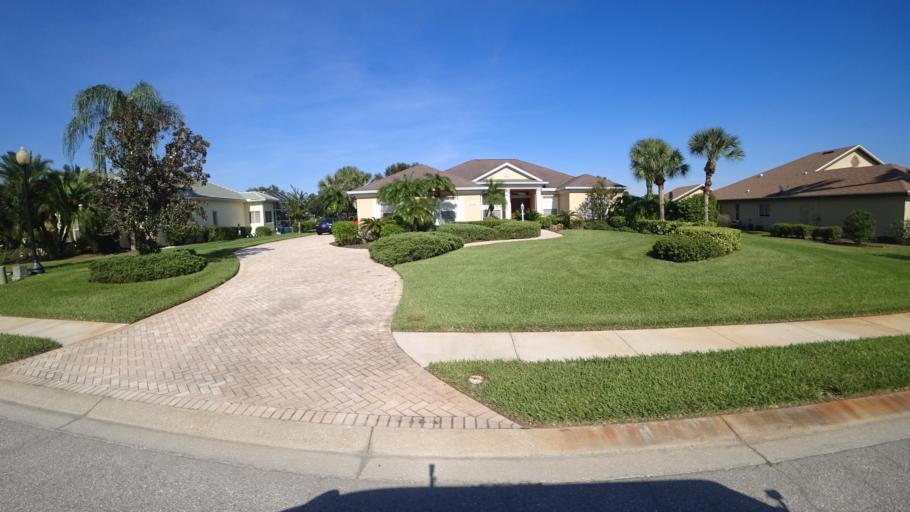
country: US
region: Florida
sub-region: Sarasota County
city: The Meadows
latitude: 27.4064
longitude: -82.4417
